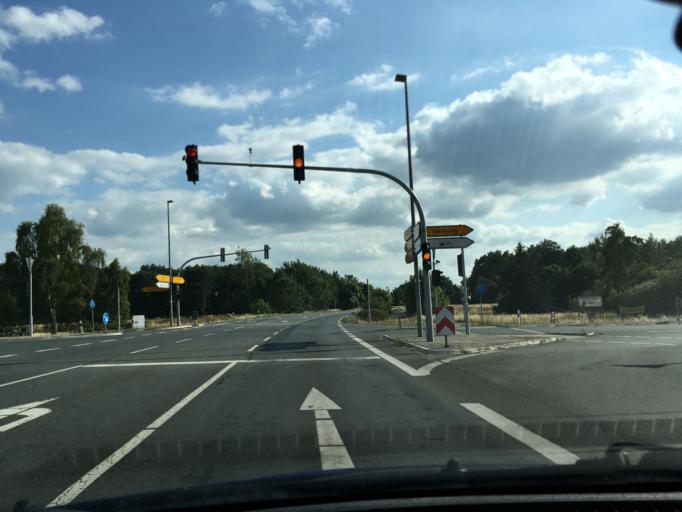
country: DE
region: Lower Saxony
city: Dannenberg
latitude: 53.0996
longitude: 11.1194
